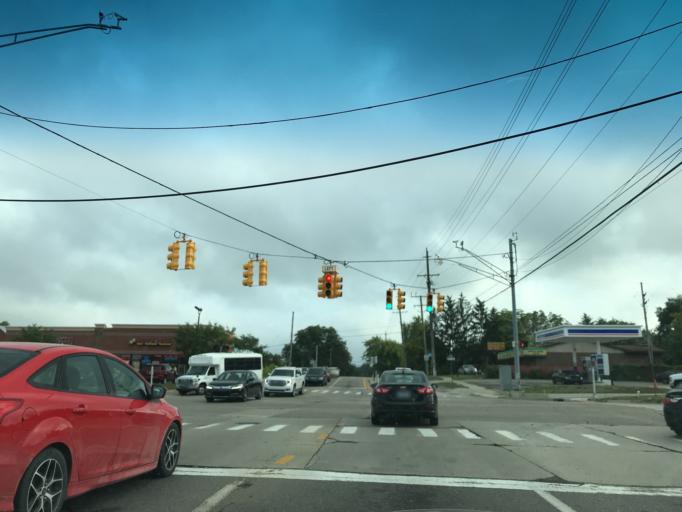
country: US
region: Michigan
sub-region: Washtenaw County
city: Ypsilanti
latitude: 42.2504
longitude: -83.6611
